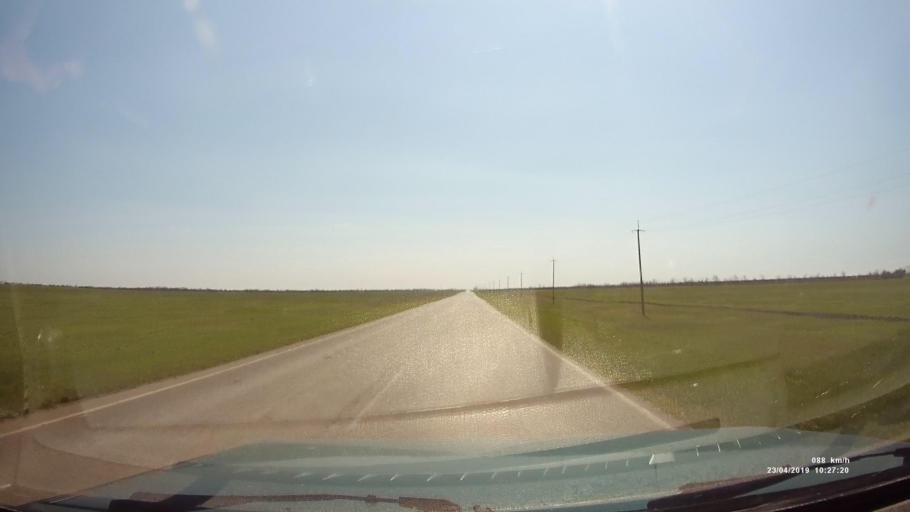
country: RU
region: Kalmykiya
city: Yashalta
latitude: 46.6146
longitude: 42.4894
